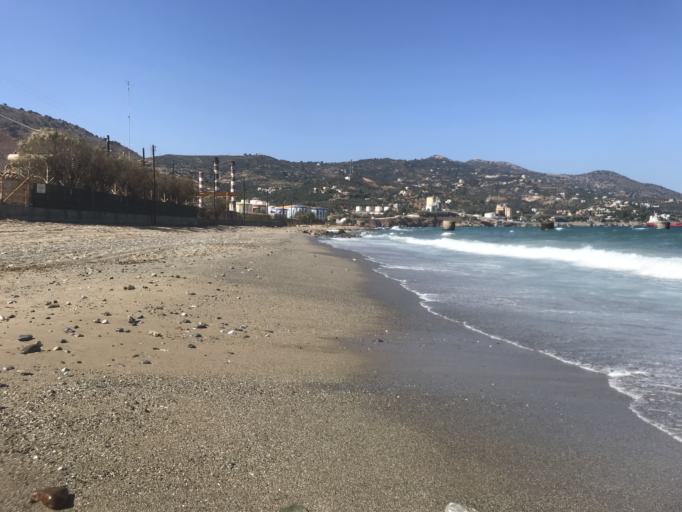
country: GR
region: Crete
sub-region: Nomos Irakleiou
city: Gazi
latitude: 35.3414
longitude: 25.0546
